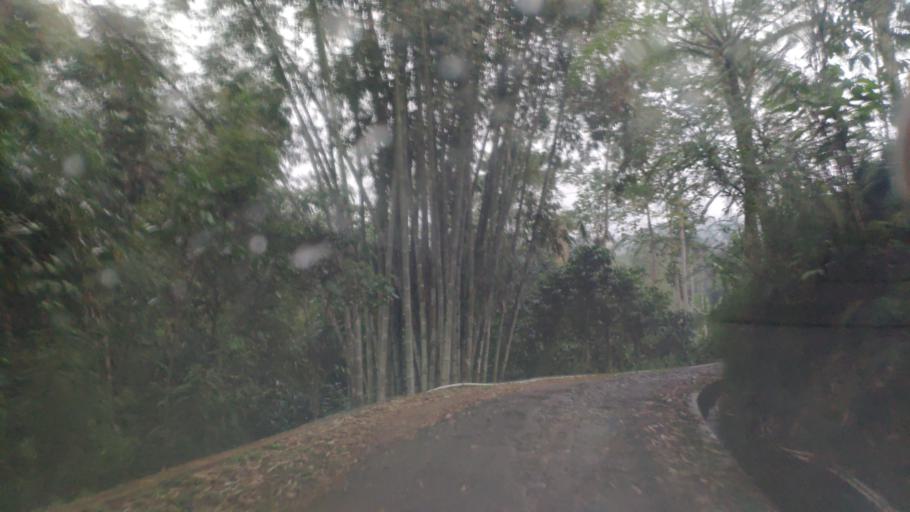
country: ID
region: Central Java
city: Wonosobo
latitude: -7.2802
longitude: 109.7301
